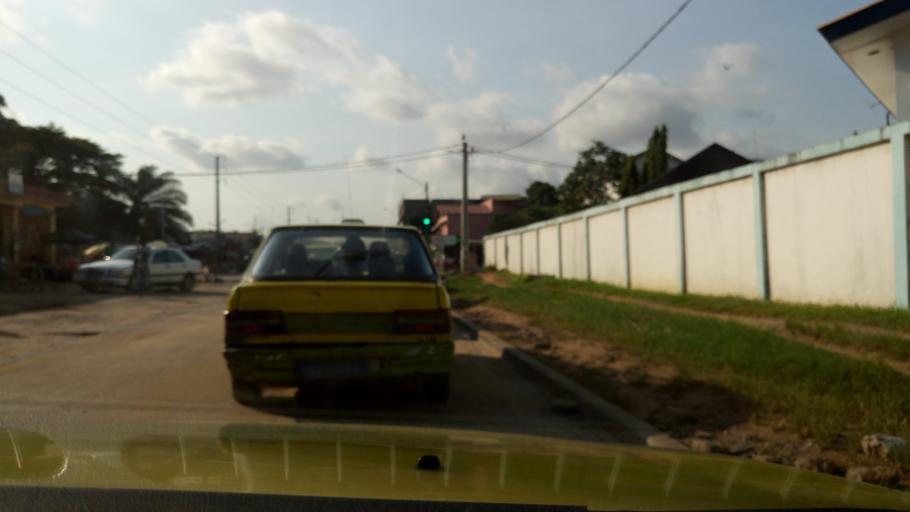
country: CI
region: Lagunes
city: Abidjan
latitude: 5.3629
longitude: -3.9625
